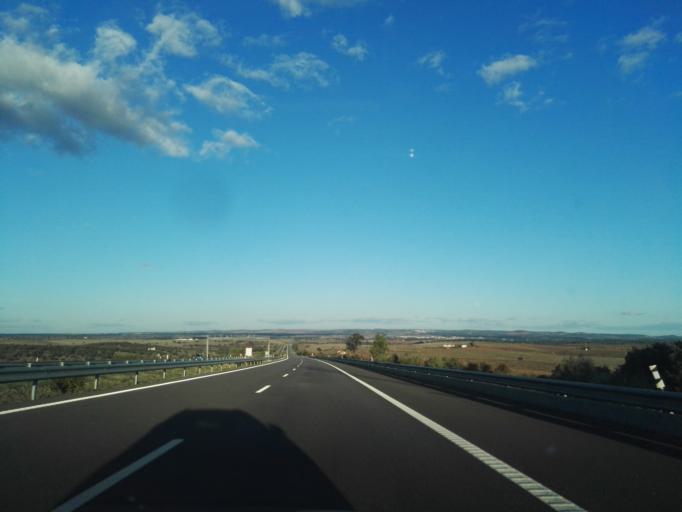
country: PT
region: Evora
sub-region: Borba
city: Borba
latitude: 38.8227
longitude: -7.4438
